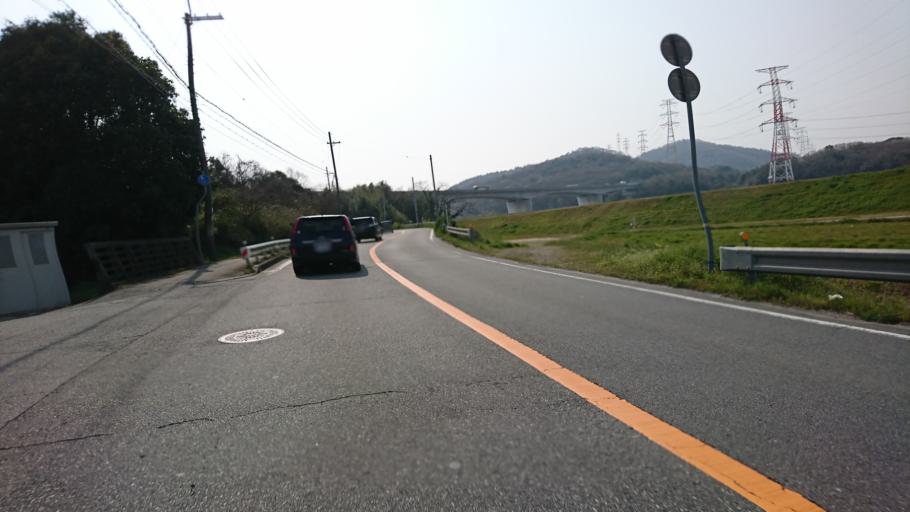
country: JP
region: Hyogo
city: Ono
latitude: 34.8122
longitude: 134.9338
